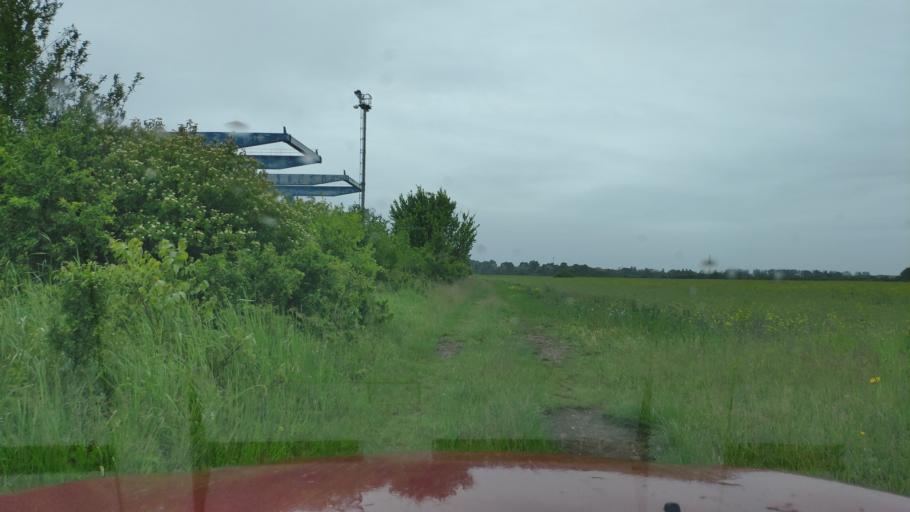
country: SK
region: Kosicky
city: Cierna nad Tisou
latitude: 48.4137
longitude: 22.0205
